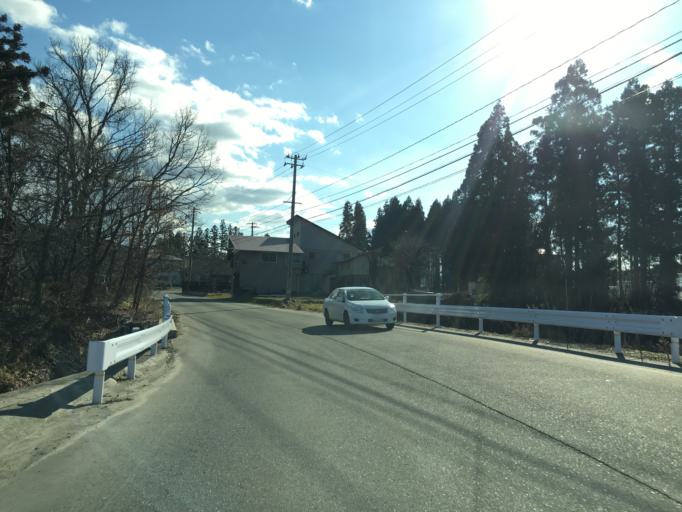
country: JP
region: Yamagata
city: Nagai
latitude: 38.0044
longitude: 140.0234
